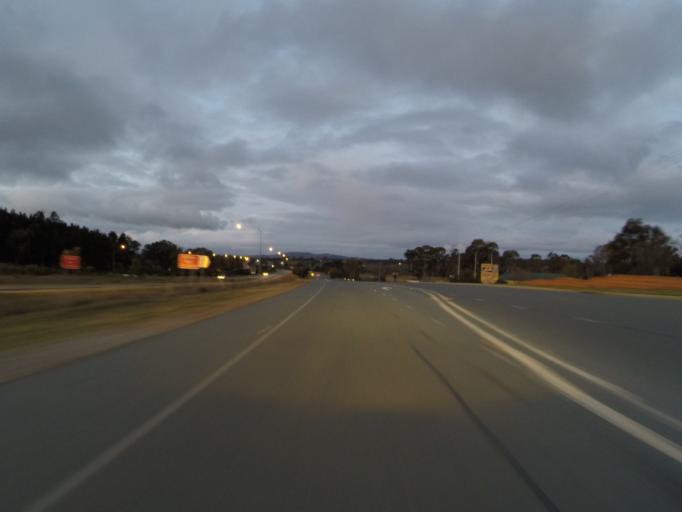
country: AU
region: Australian Capital Territory
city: Kaleen
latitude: -35.2022
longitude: 149.2117
